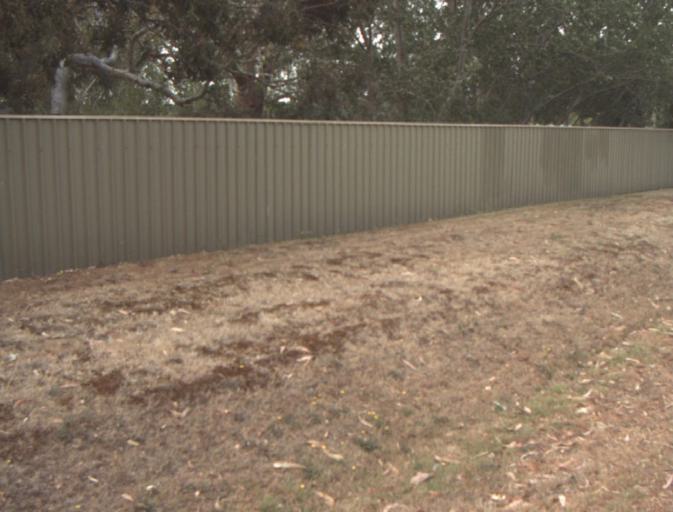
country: AU
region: Tasmania
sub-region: Launceston
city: Mayfield
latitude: -41.3322
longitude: 147.0545
